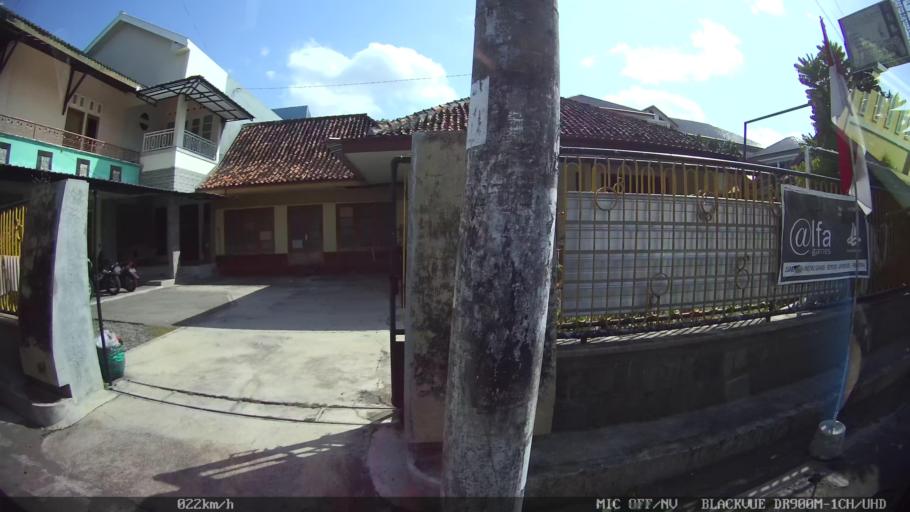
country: ID
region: Daerah Istimewa Yogyakarta
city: Yogyakarta
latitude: -7.8209
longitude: 110.3707
